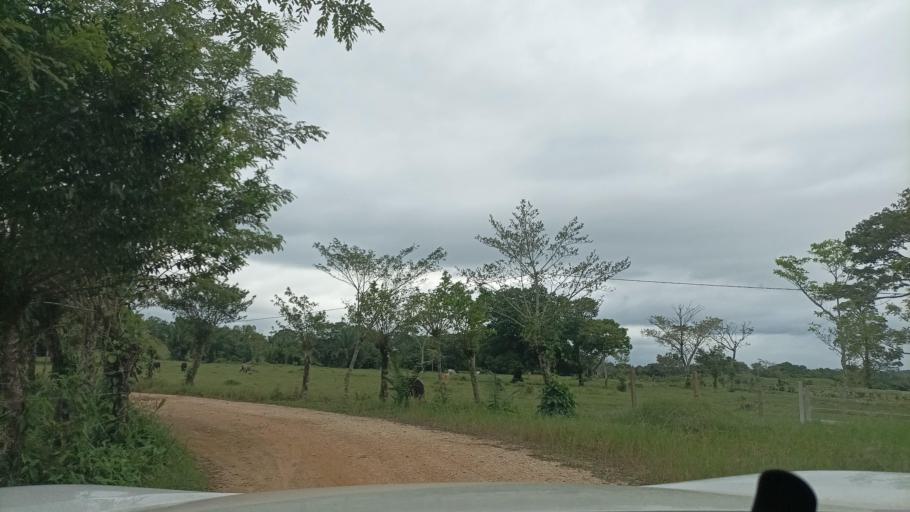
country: MX
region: Veracruz
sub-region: Uxpanapa
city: Poblado Cinco
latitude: 17.5030
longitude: -94.5634
